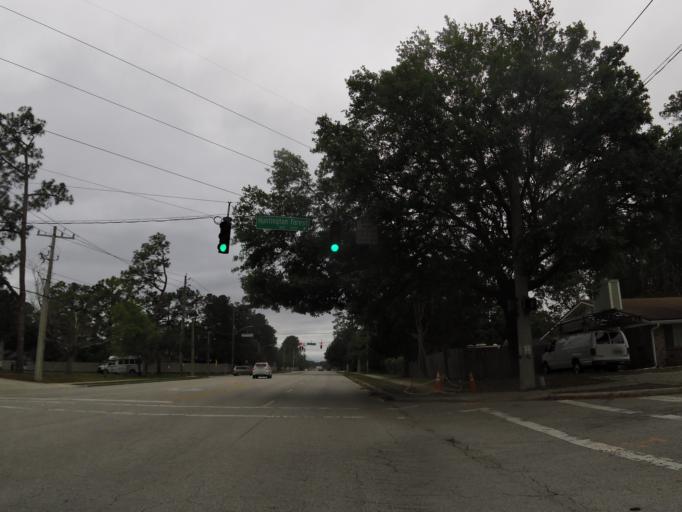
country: US
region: Florida
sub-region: Saint Johns County
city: Fruit Cove
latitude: 30.1957
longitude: -81.6122
